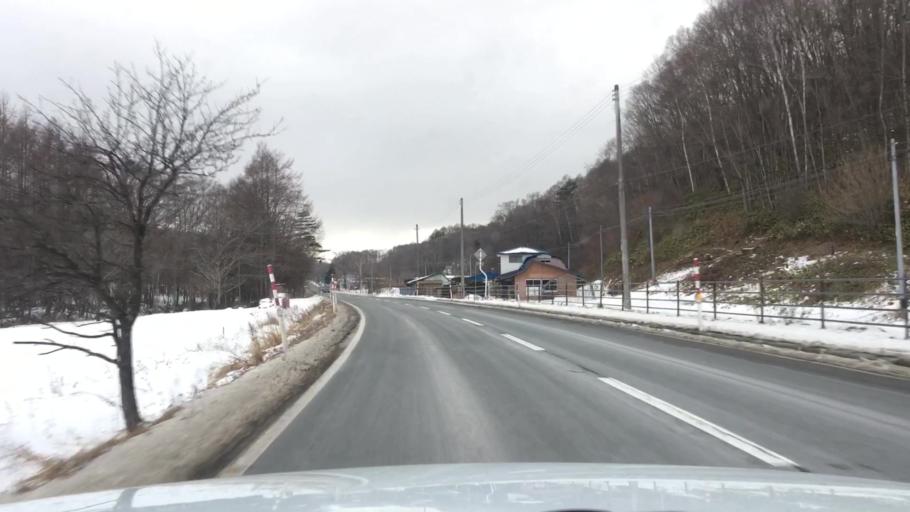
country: JP
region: Iwate
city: Morioka-shi
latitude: 39.6414
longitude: 141.4206
